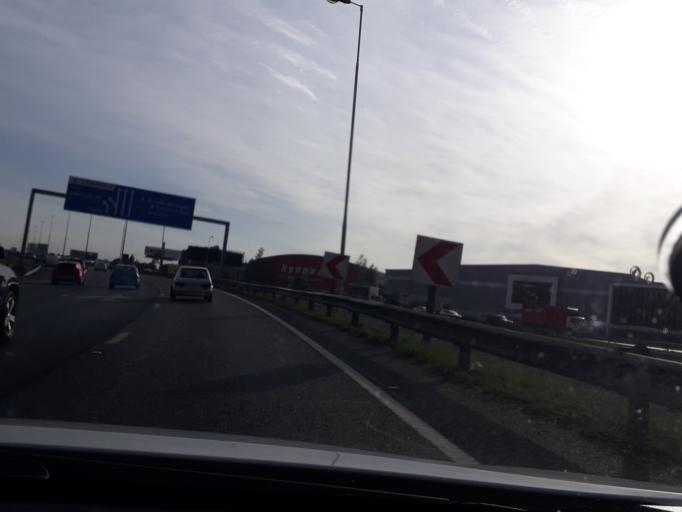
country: ZA
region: Gauteng
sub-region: City of Johannesburg Metropolitan Municipality
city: Modderfontein
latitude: -26.1630
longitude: 28.1560
